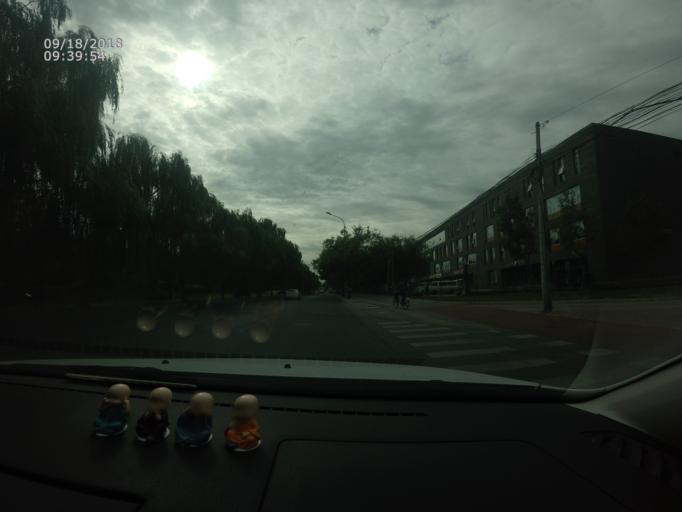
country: CN
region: Beijing
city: Xibeiwang
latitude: 40.0686
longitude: 116.2392
